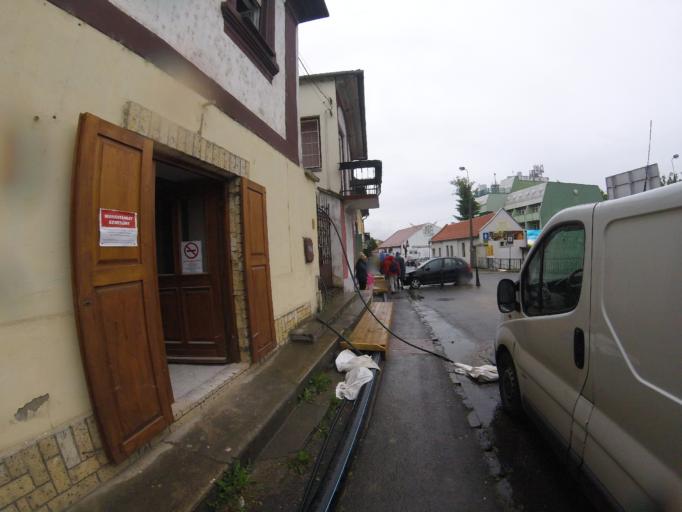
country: HU
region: Borsod-Abauj-Zemplen
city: Tokaj
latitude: 48.1218
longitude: 21.4123
